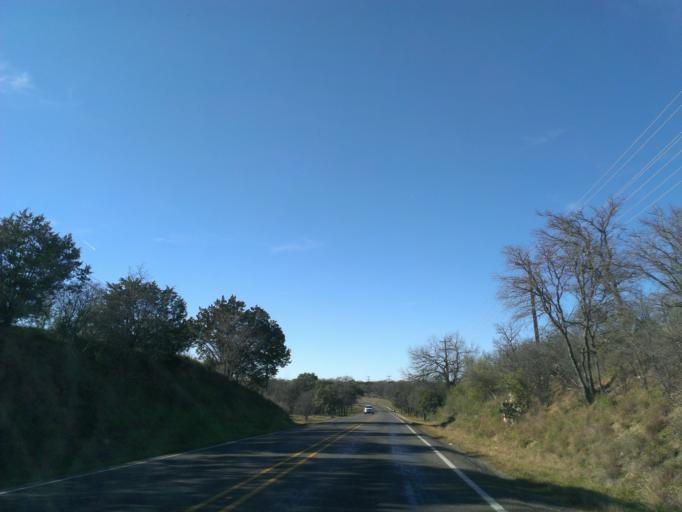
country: US
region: Texas
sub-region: Burnet County
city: Cottonwood Shores
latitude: 30.5474
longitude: -98.3117
